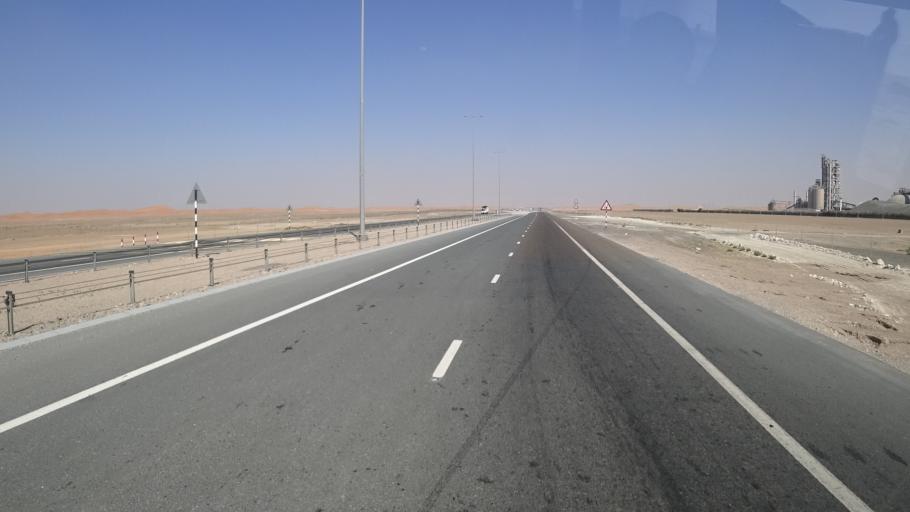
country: AE
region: Abu Dhabi
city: Al Ain
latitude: 24.0086
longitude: 55.4286
